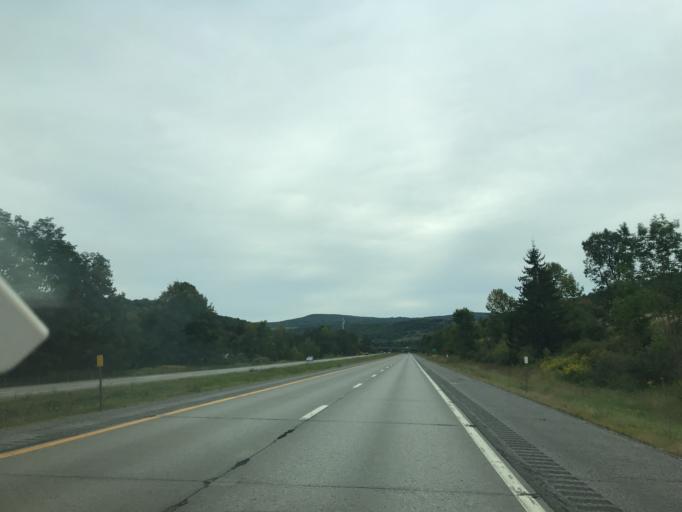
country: US
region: New York
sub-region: Schoharie County
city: Cobleskill
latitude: 42.6419
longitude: -74.5820
